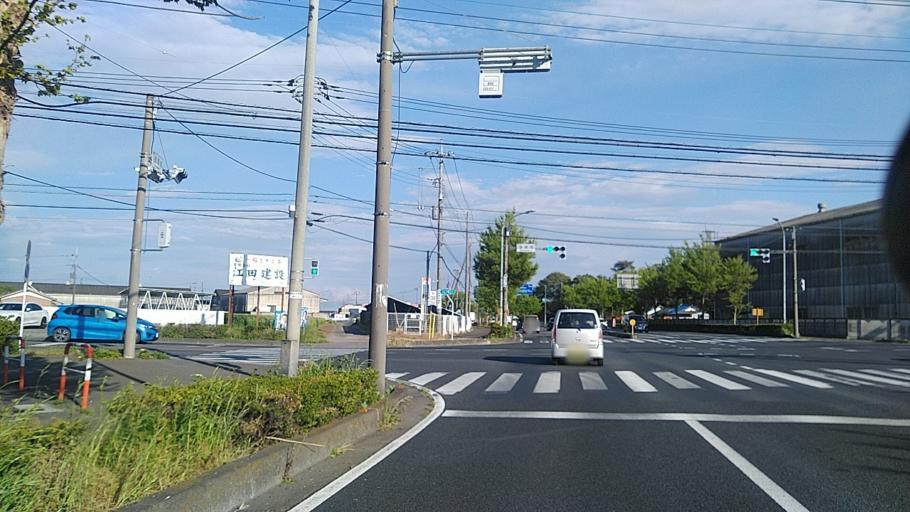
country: JP
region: Gunma
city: Tatebayashi
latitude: 36.2395
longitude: 139.4671
